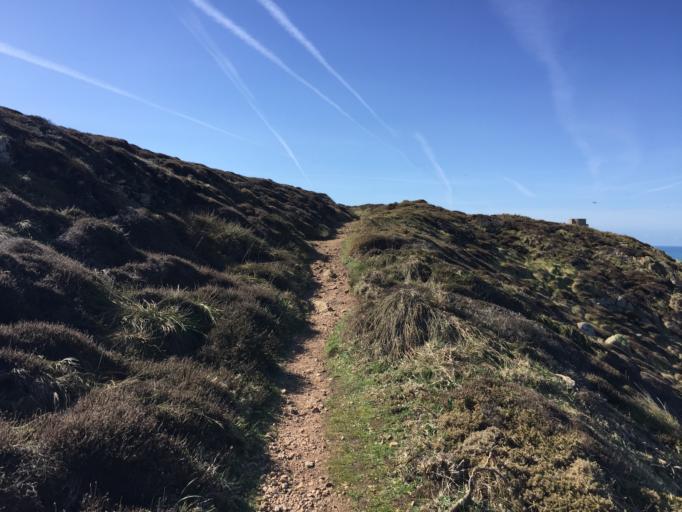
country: JE
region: St Helier
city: Saint Helier
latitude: 49.2541
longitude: -2.2500
